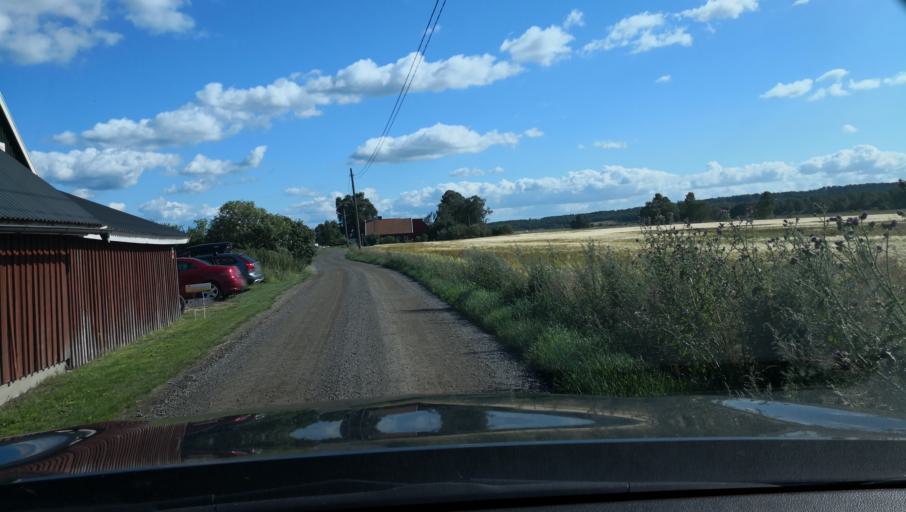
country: SE
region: Skane
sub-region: Kristianstads Kommun
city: Degeberga
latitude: 55.8096
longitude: 14.1891
